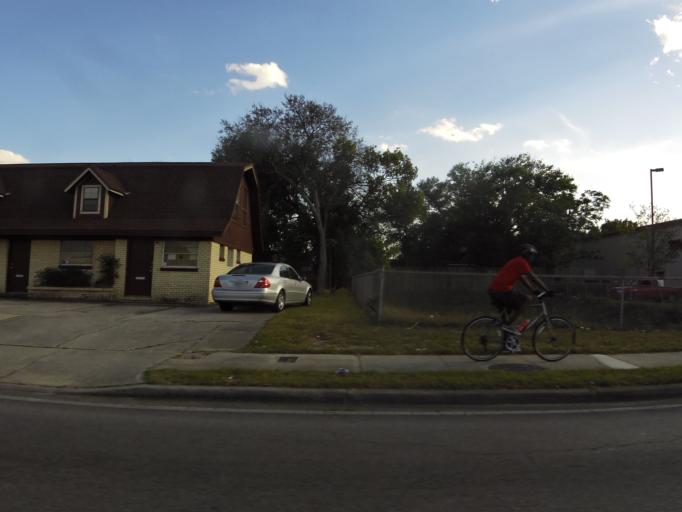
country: US
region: Florida
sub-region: Duval County
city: Jacksonville
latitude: 30.3520
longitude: -81.5766
